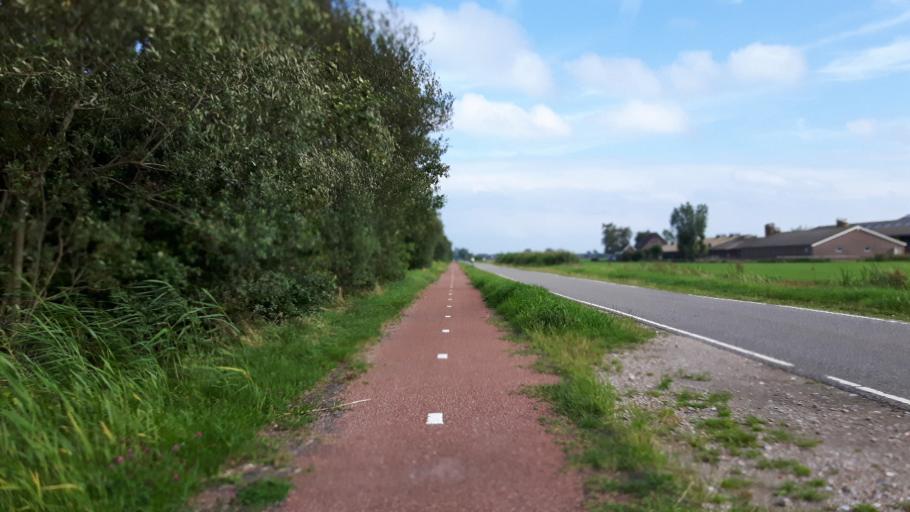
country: NL
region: South Holland
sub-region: Gemeente Nieuwkoop
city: Nieuwkoop
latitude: 52.1245
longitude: 4.8180
